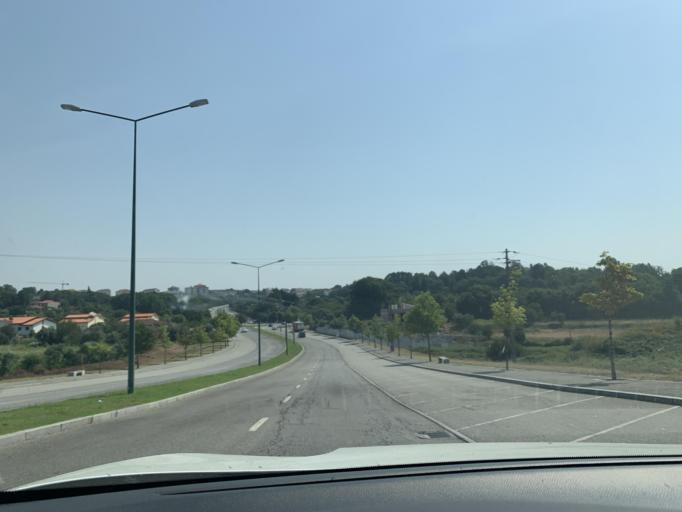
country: PT
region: Viseu
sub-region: Viseu
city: Viseu
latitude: 40.6469
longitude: -7.9043
